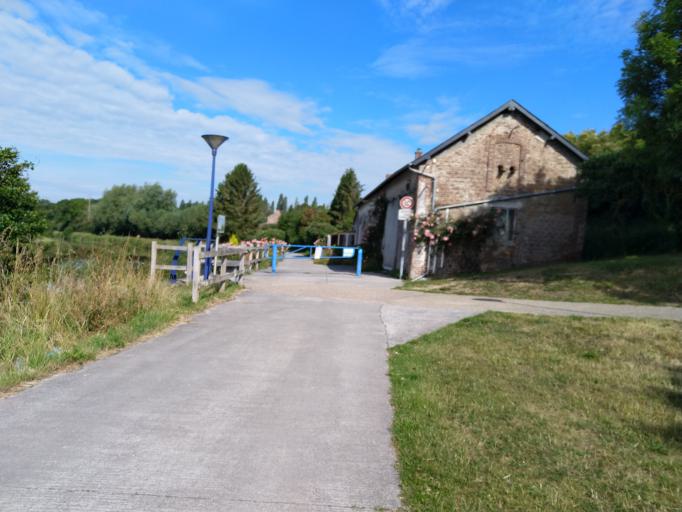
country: FR
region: Nord-Pas-de-Calais
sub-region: Departement du Nord
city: Rousies
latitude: 50.2848
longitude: 4.0131
